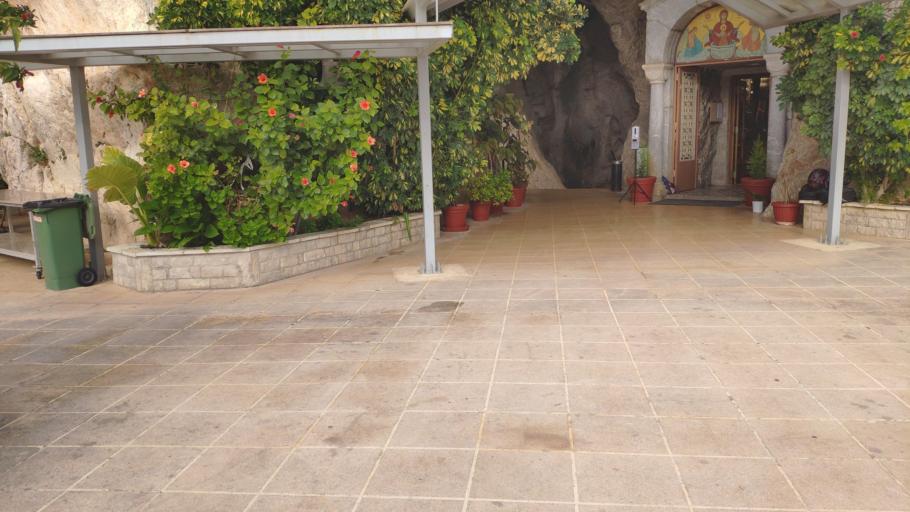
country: GR
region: Peloponnese
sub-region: Nomos Argolidos
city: Nea Kios
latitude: 37.5961
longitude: 22.6876
